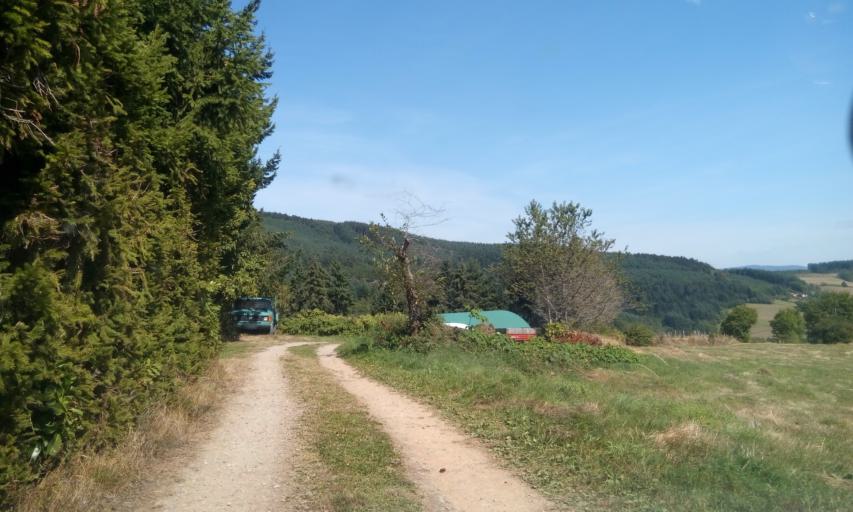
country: FR
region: Rhone-Alpes
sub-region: Departement du Rhone
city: Cublize
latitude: 45.9998
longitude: 4.4311
